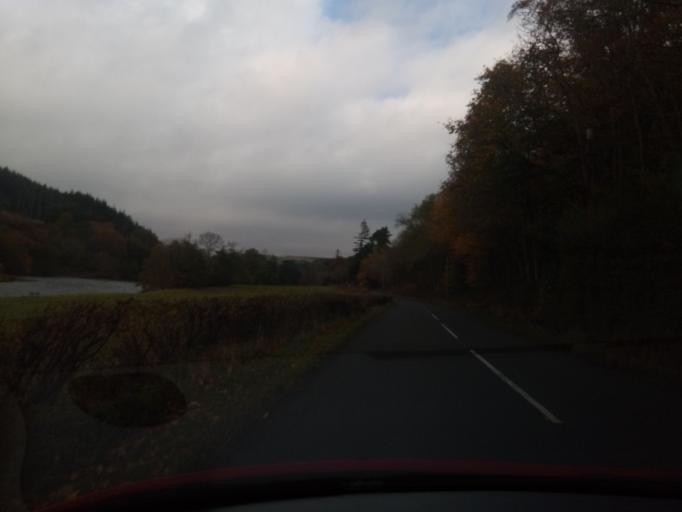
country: GB
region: Scotland
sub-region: The Scottish Borders
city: Selkirk
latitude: 55.6010
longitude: -2.8693
